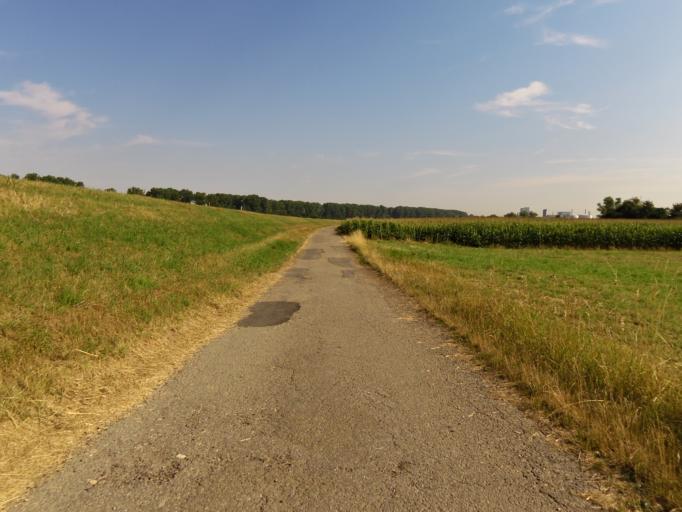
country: DE
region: Hesse
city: Lampertheim
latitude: 49.5567
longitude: 8.4209
